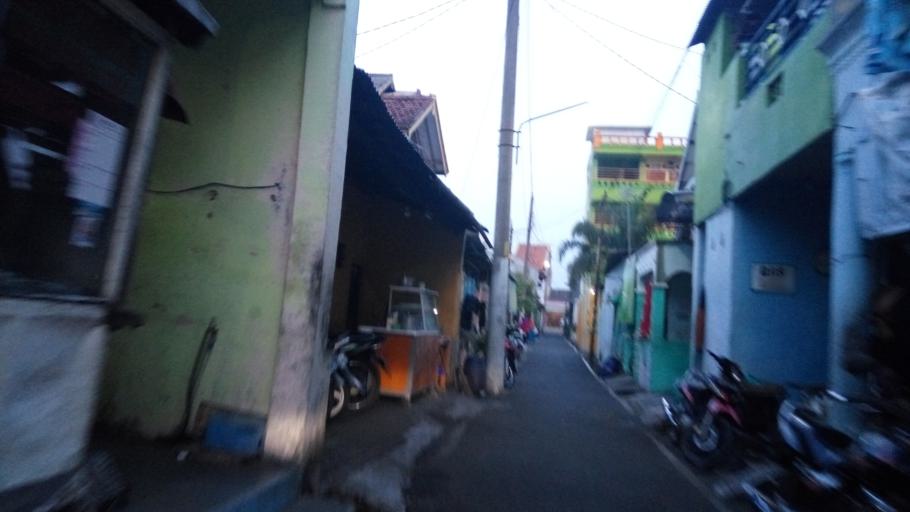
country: ID
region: Central Java
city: Semarang
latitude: -6.9846
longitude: 110.4049
